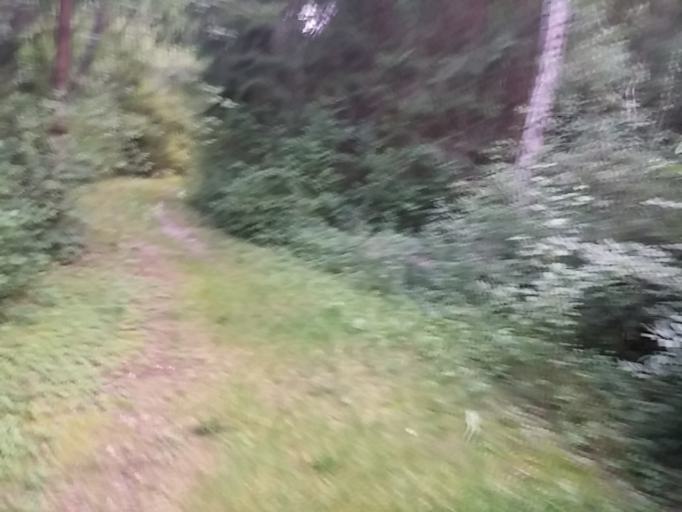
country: DE
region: Baden-Wuerttemberg
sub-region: Tuebingen Region
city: Aitrach
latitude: 47.9349
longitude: 10.0870
